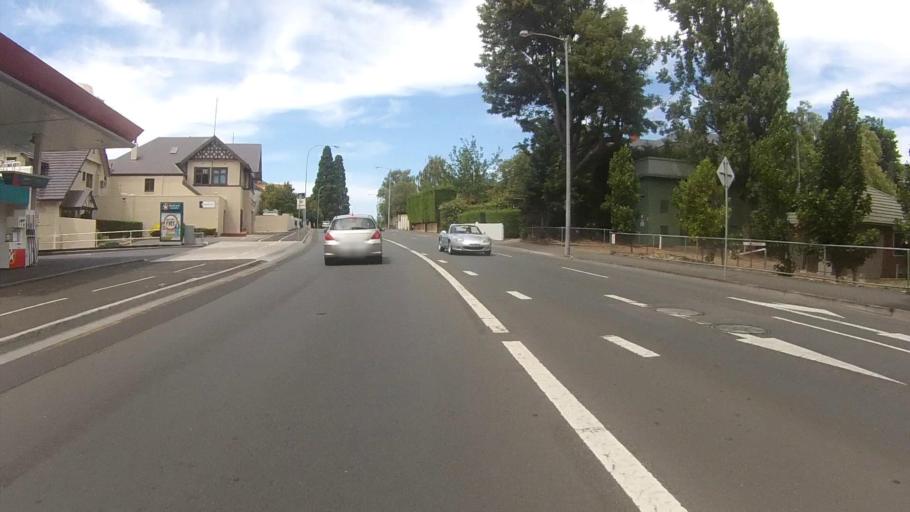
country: AU
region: Tasmania
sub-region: Hobart
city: Sandy Bay
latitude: -42.9023
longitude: 147.3344
